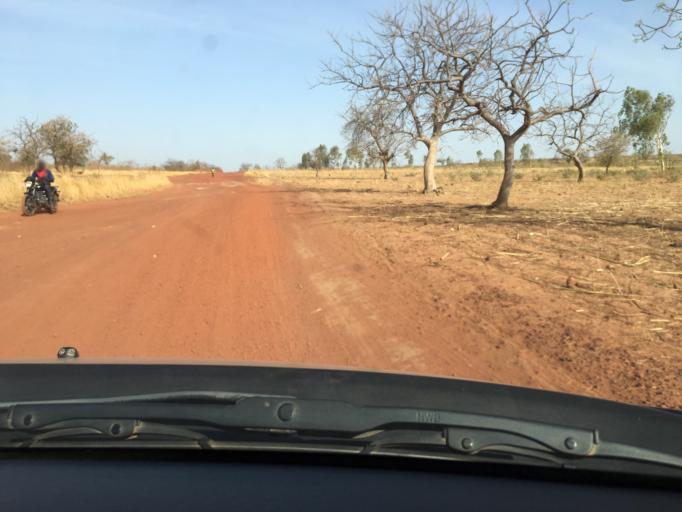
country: BF
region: Plateau-Central
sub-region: Province du Kourweogo
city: Bousse
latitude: 12.5600
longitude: -1.8998
